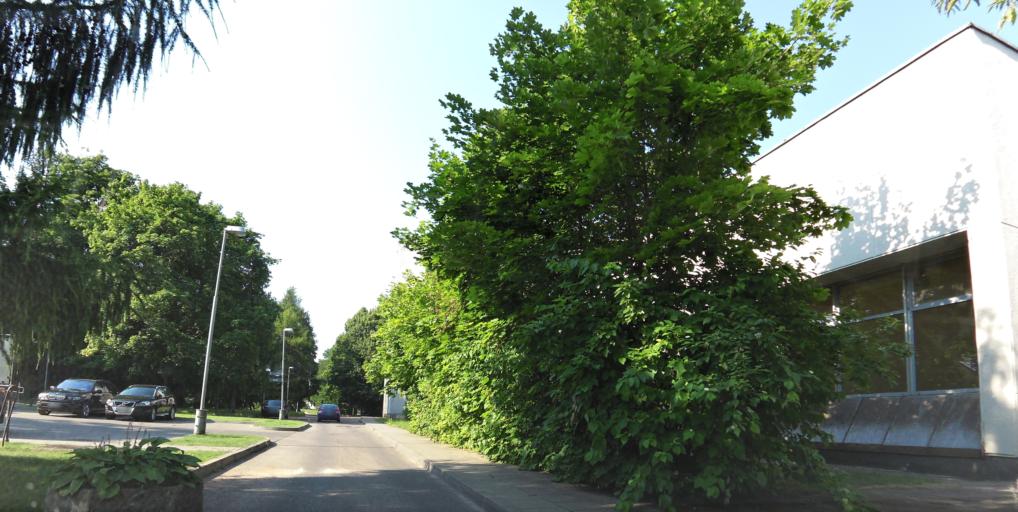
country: LT
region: Vilnius County
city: Rasos
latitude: 54.6971
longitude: 25.3017
